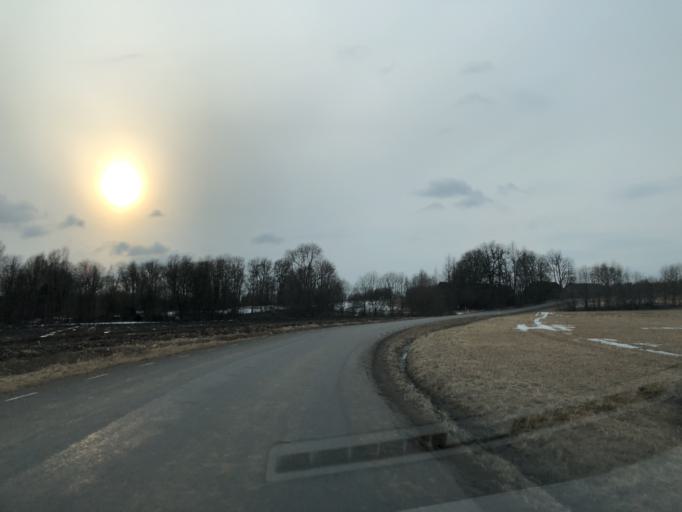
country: EE
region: Paernumaa
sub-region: Vaendra vald (alev)
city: Vandra
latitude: 58.6936
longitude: 24.9394
